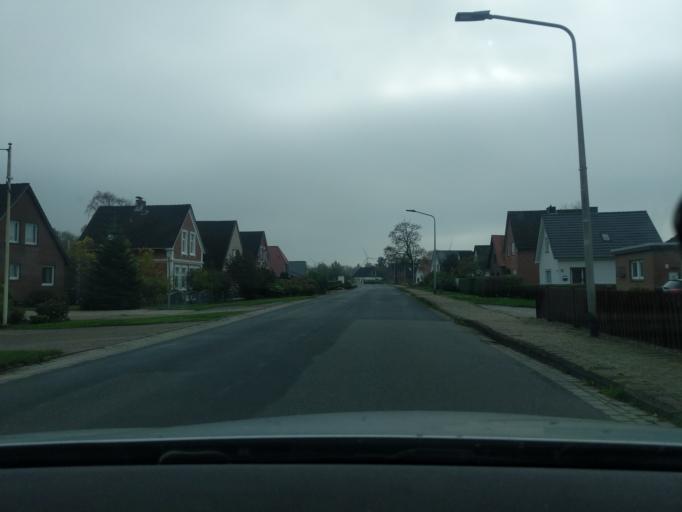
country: DE
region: Lower Saxony
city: Cuxhaven
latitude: 53.8387
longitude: 8.7275
